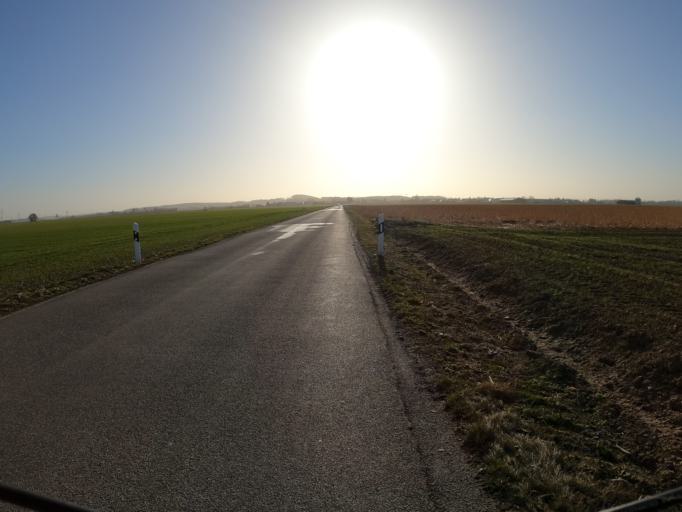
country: DE
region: Bavaria
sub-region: Swabia
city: Nersingen
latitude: 48.4045
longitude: 10.1199
